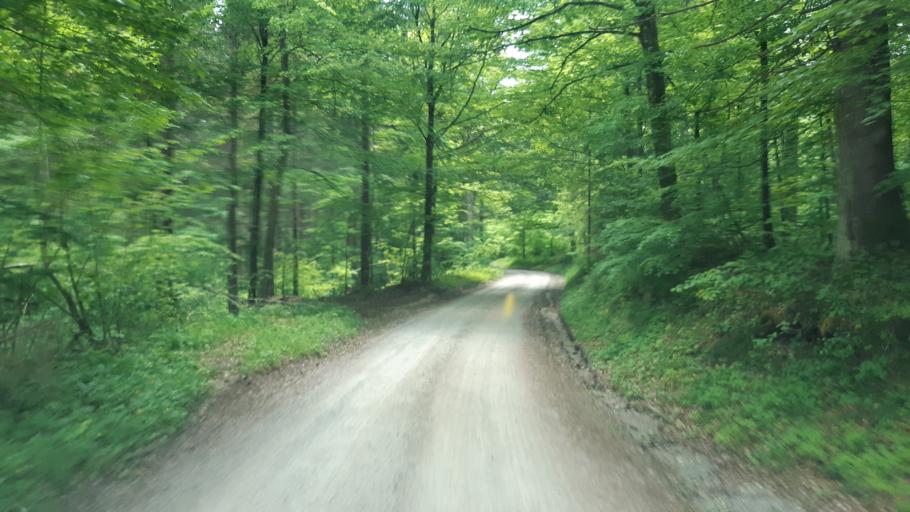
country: SI
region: Dolenjske Toplice
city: Dolenjske Toplice
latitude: 45.6145
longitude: 15.0167
